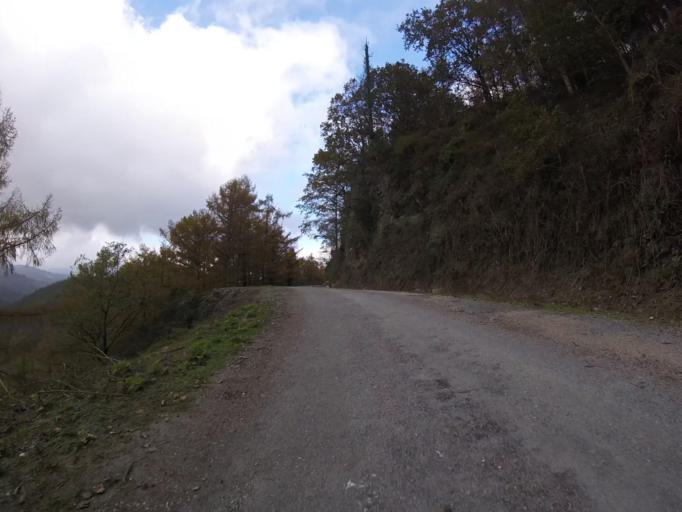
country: ES
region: Navarre
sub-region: Provincia de Navarra
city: Goizueta
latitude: 43.2123
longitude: -1.8564
